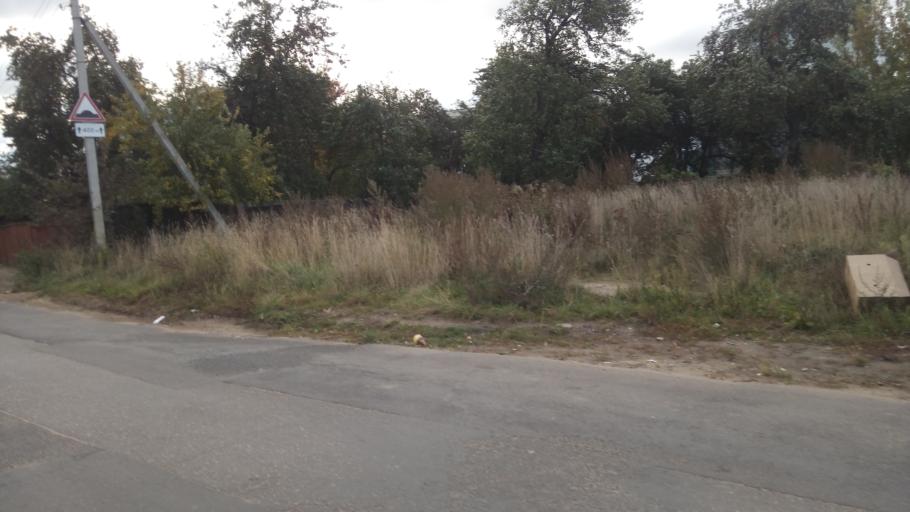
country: BY
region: Minsk
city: Minsk
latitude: 53.8878
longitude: 27.5562
